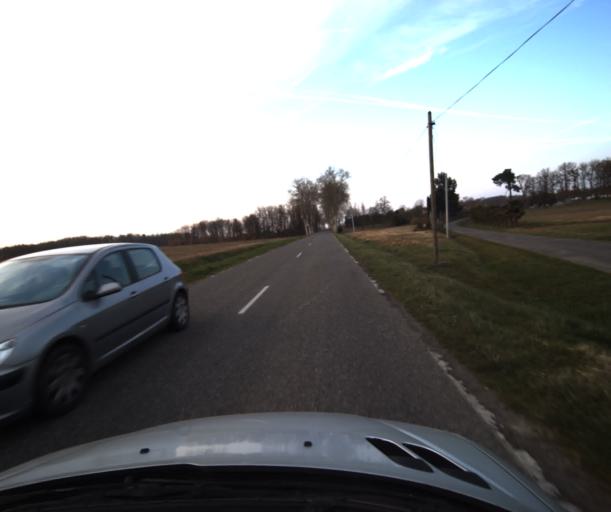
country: FR
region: Midi-Pyrenees
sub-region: Departement de la Haute-Garonne
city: Fronton
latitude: 43.8774
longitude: 1.3780
